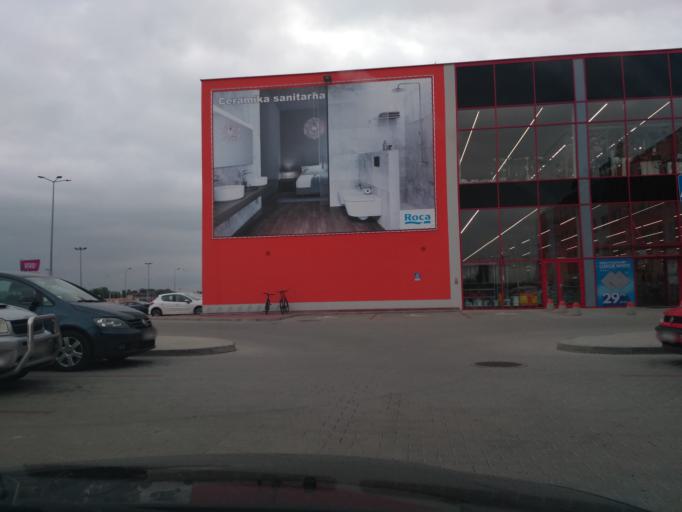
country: PL
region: Subcarpathian Voivodeship
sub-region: Krosno
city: Krosno
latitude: 49.6744
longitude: 21.7786
